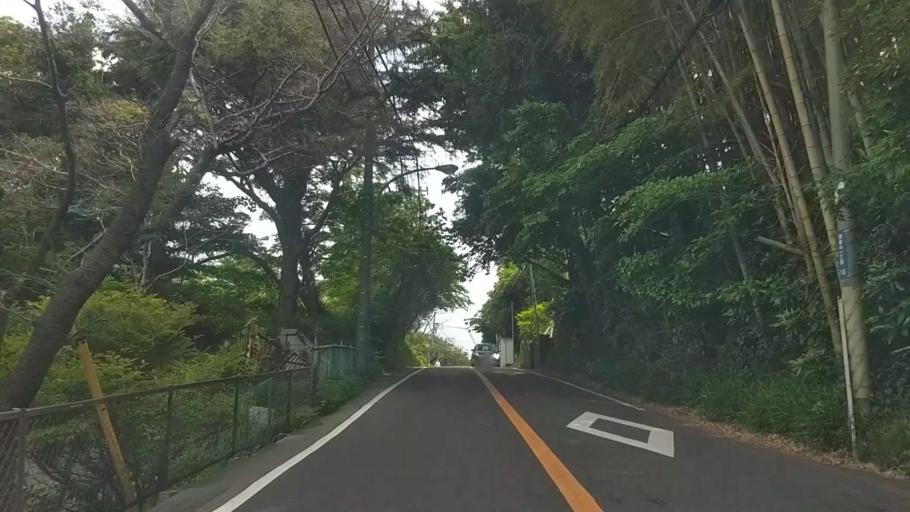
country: JP
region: Kanagawa
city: Kamakura
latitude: 35.3183
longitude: 139.5197
